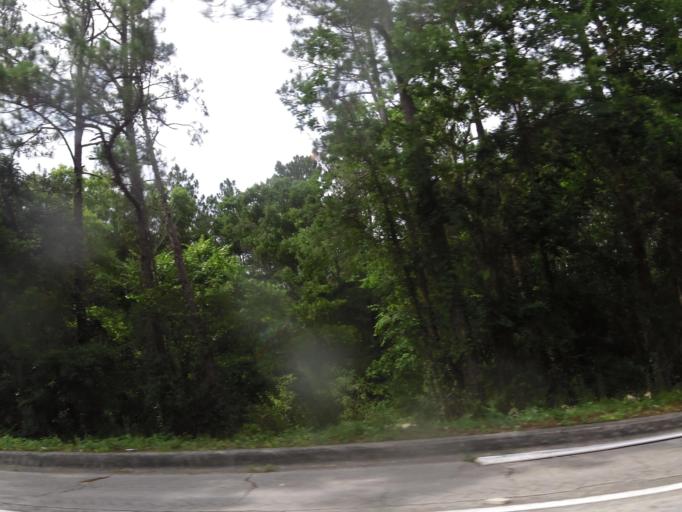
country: US
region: Florida
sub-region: Saint Johns County
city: Saint Augustine South
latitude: 29.8616
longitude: -81.3932
